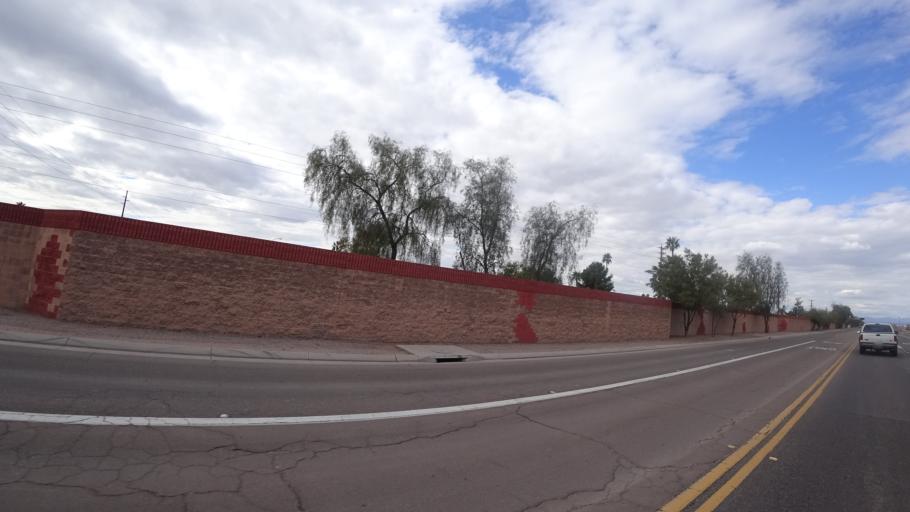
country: US
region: Arizona
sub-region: Maricopa County
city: Scottsdale
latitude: 33.5136
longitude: -111.8916
